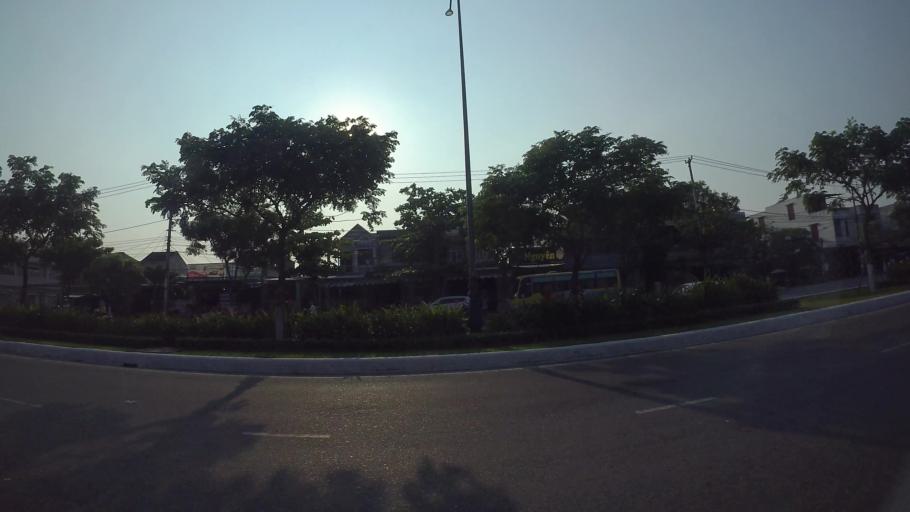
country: VN
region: Da Nang
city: Ngu Hanh Son
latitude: 15.9748
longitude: 108.2548
